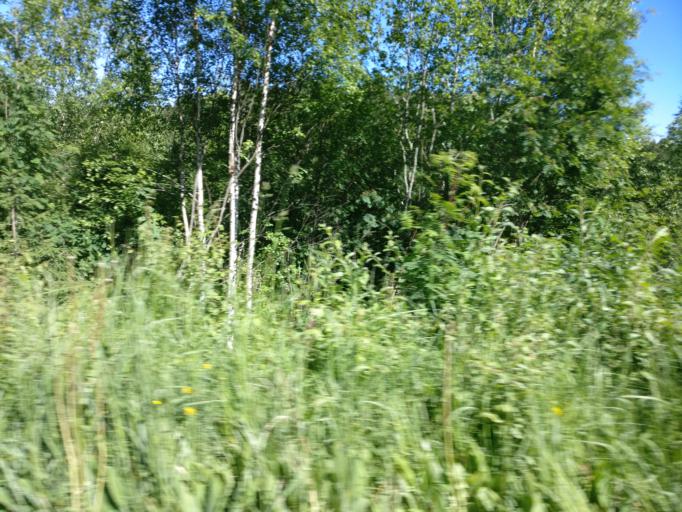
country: FI
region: Southern Savonia
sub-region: Savonlinna
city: Rantasalmi
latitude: 62.1623
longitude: 28.2443
